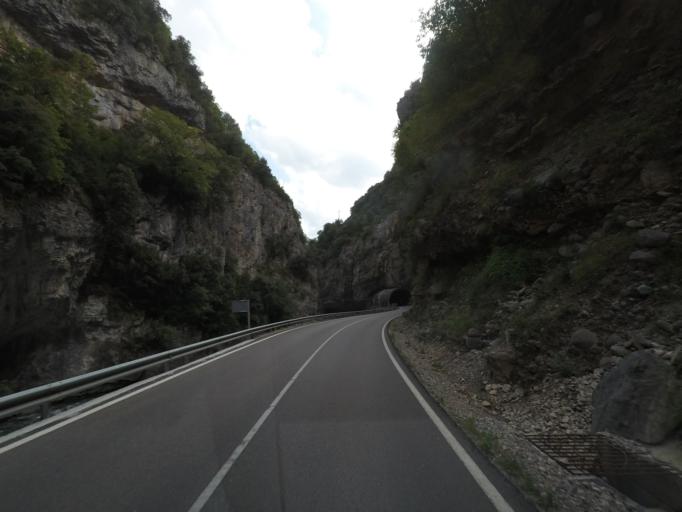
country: ES
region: Aragon
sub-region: Provincia de Huesca
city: Puertolas
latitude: 42.5596
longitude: 0.2045
